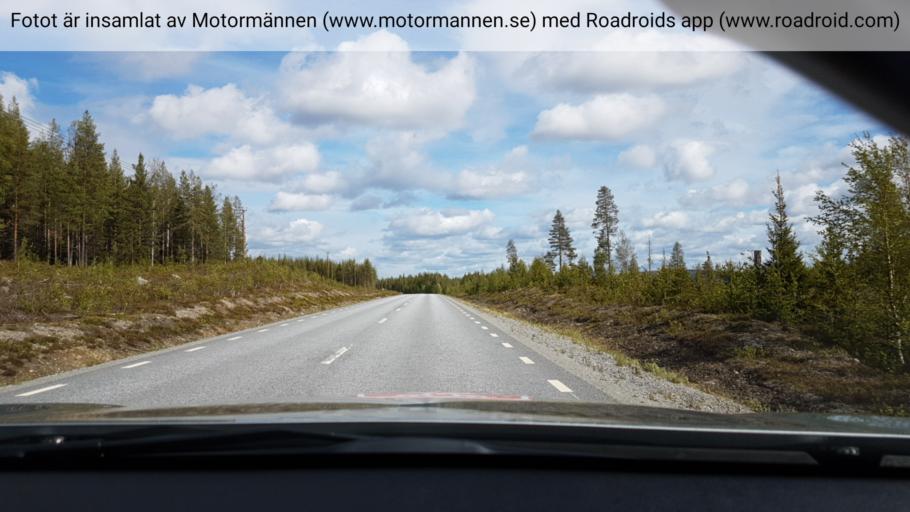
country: SE
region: Vaesterbotten
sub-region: Asele Kommun
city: Insjon
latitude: 64.1480
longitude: 17.9100
